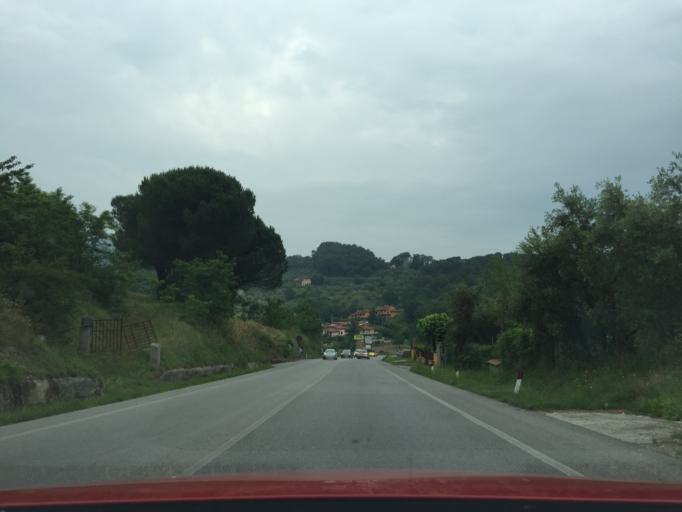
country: IT
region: Tuscany
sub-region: Provincia di Pistoia
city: Serravalle Pistoiese
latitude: 43.9069
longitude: 10.8384
